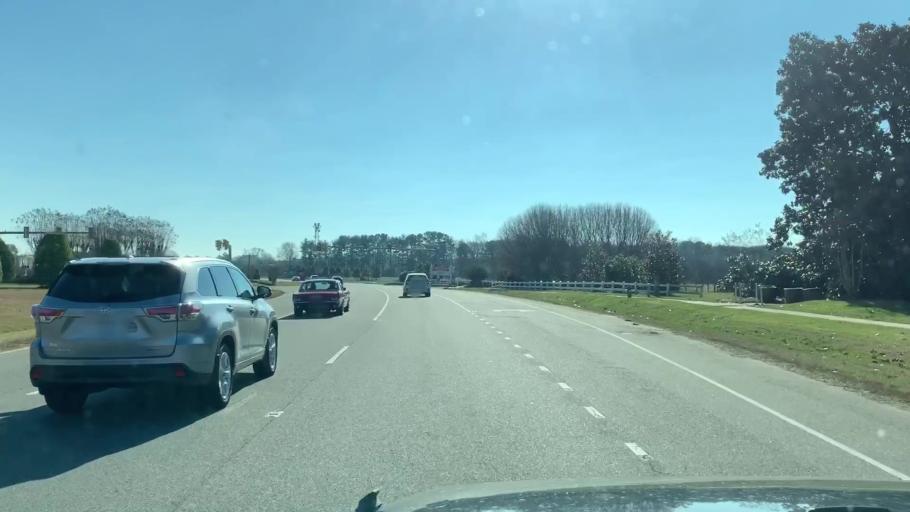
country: US
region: Virginia
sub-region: James City County
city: Williamsburg
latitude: 37.3509
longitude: -76.7633
